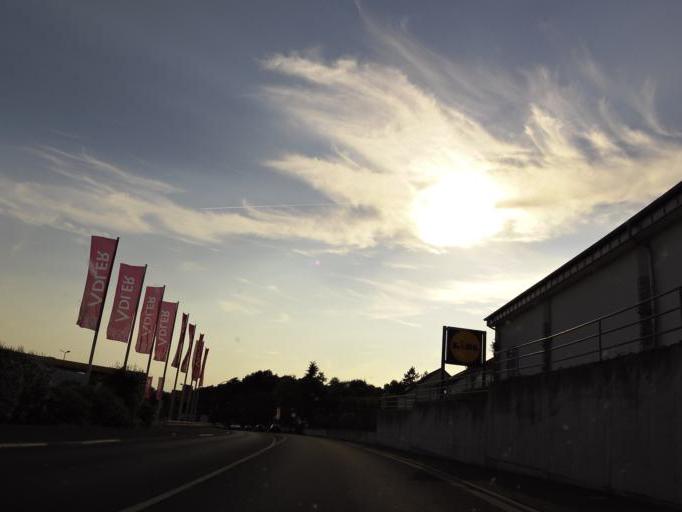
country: DE
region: Bavaria
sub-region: Regierungsbezirk Unterfranken
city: Haibach
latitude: 49.9645
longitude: 9.1907
